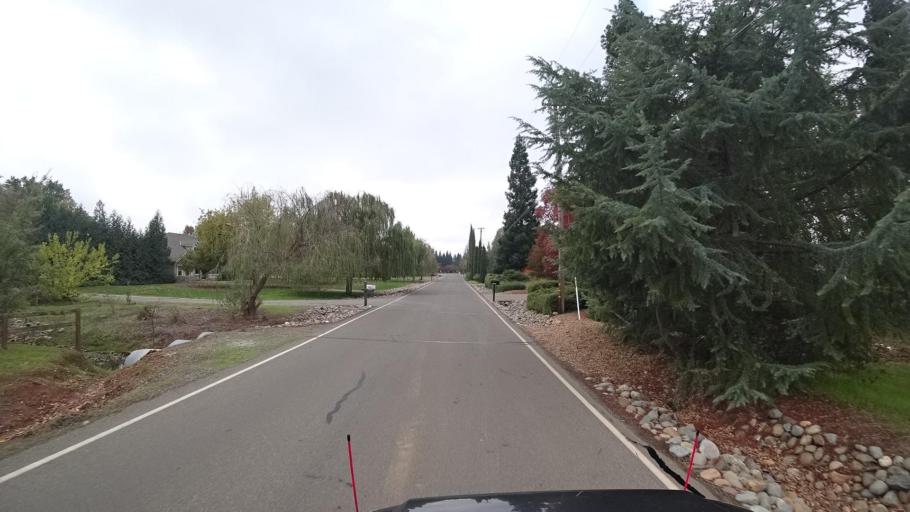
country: US
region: California
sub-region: Sacramento County
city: Wilton
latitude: 38.4499
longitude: -121.2990
